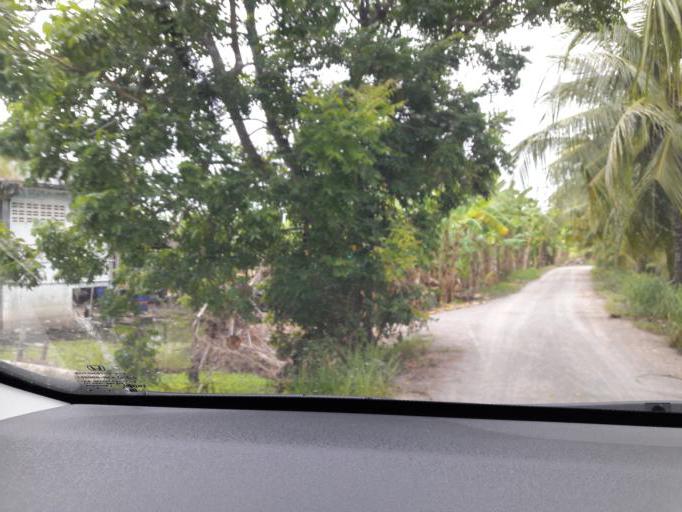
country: TH
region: Ratchaburi
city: Damnoen Saduak
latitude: 13.5587
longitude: 100.0272
